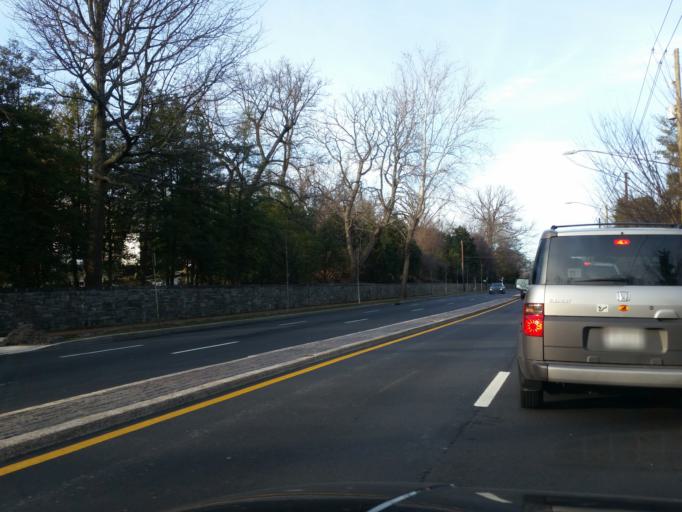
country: US
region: Maryland
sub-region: Montgomery County
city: Chevy Chase
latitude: 38.9743
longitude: -77.0772
